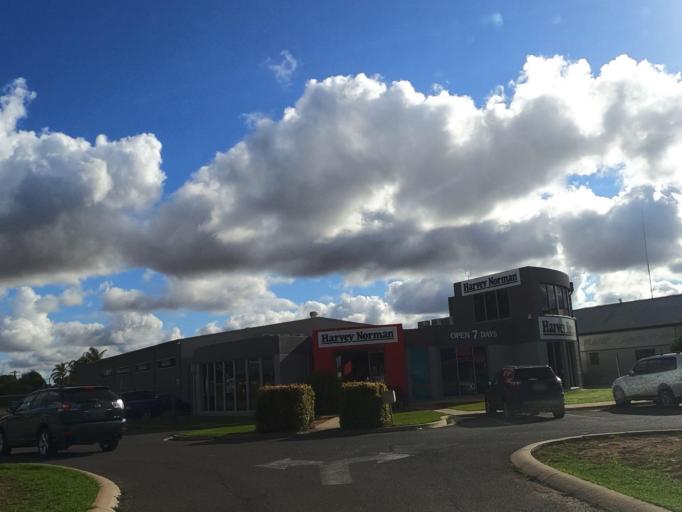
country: AU
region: Victoria
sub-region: Swan Hill
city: Swan Hill
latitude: -35.3322
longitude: 143.5552
